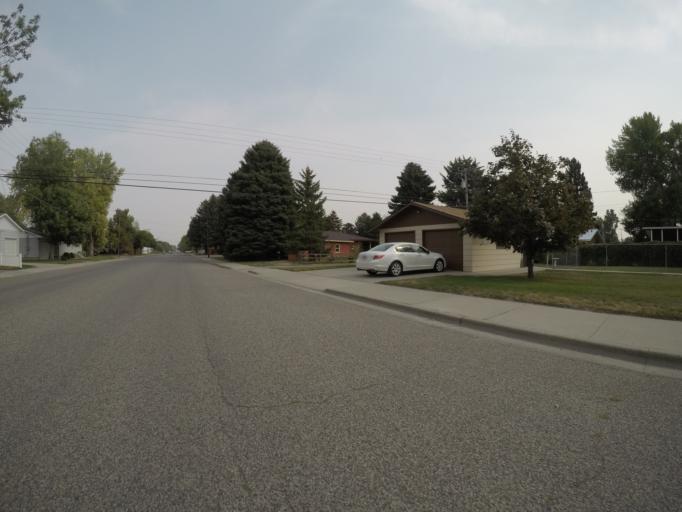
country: US
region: Montana
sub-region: Yellowstone County
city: Laurel
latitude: 45.6791
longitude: -108.7771
